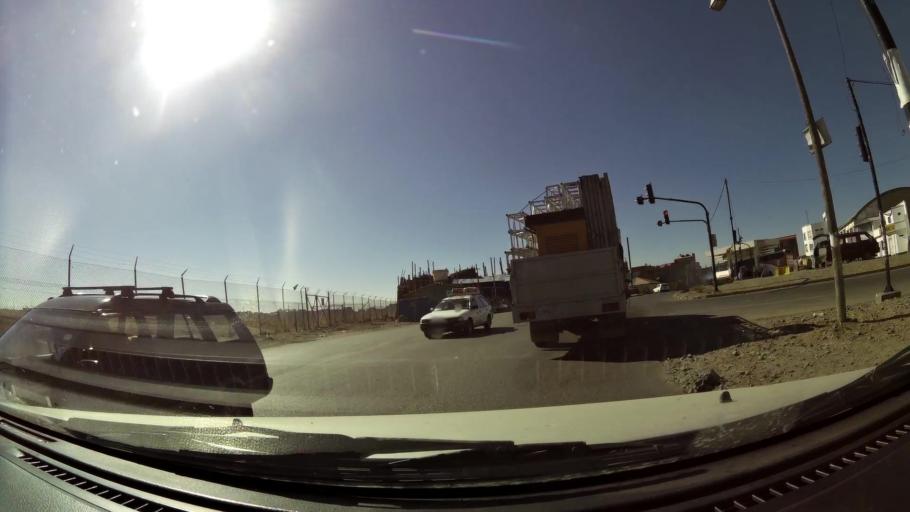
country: BO
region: La Paz
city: La Paz
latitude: -16.5163
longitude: -68.1743
